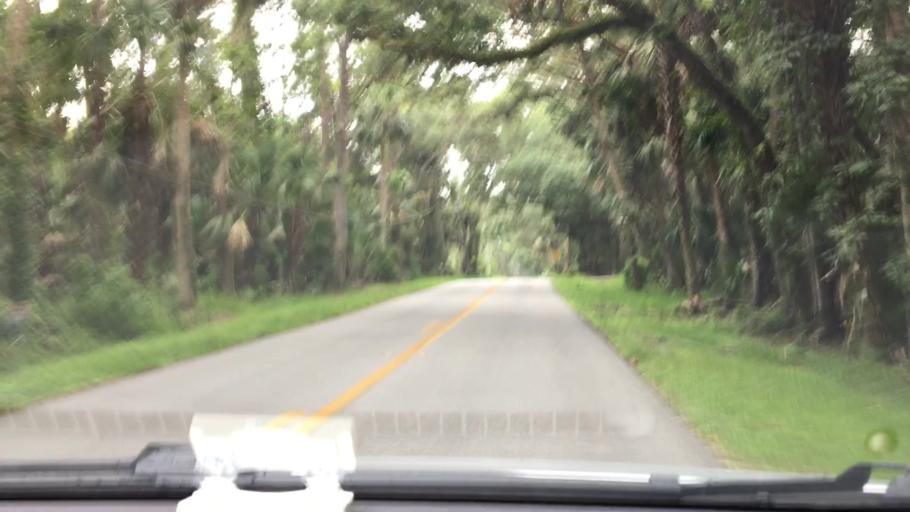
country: US
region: Florida
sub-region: Volusia County
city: Deltona
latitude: 28.8600
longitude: -81.2338
